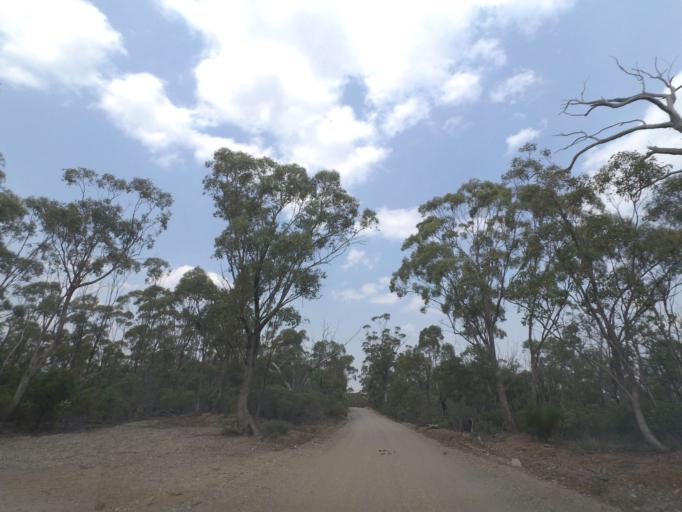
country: AU
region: Victoria
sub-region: Moorabool
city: Bacchus Marsh
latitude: -37.5996
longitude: 144.4468
